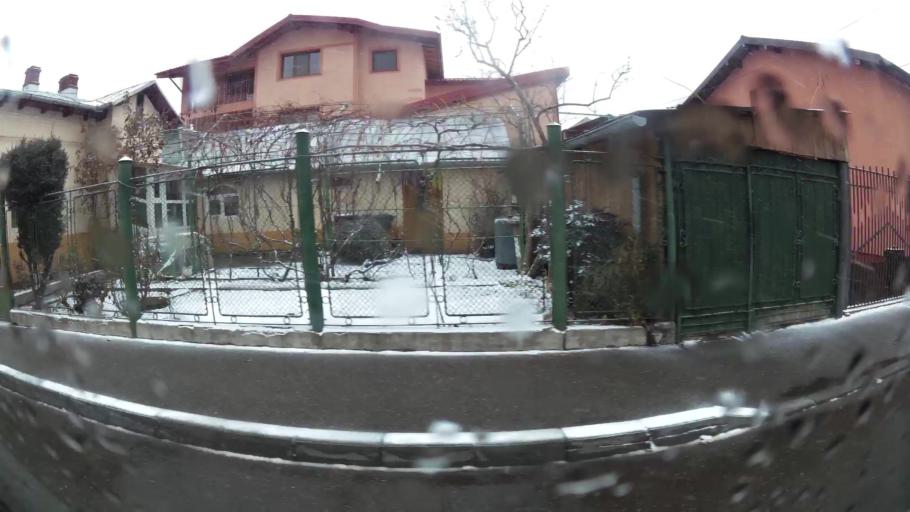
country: RO
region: Prahova
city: Ploiesti
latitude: 44.9460
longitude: 26.0055
